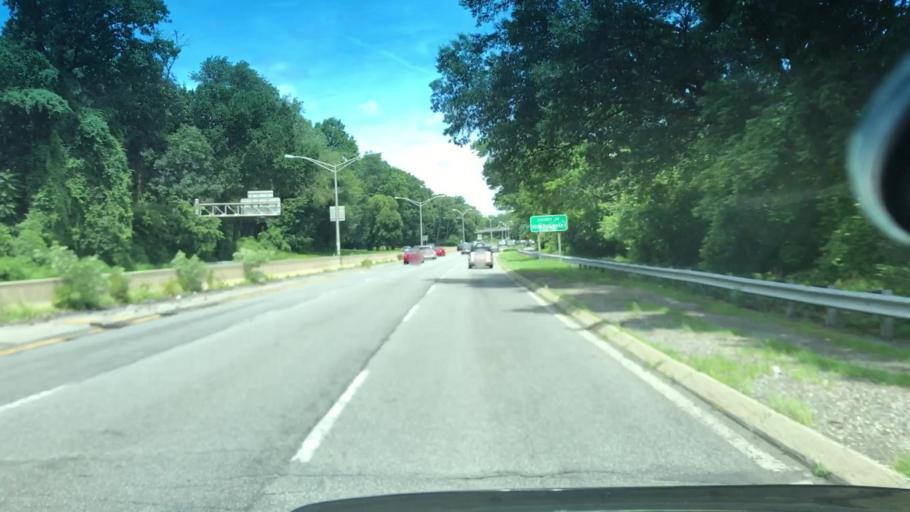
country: US
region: New York
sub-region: Westchester County
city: Mount Vernon
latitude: 40.9016
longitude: -73.8601
